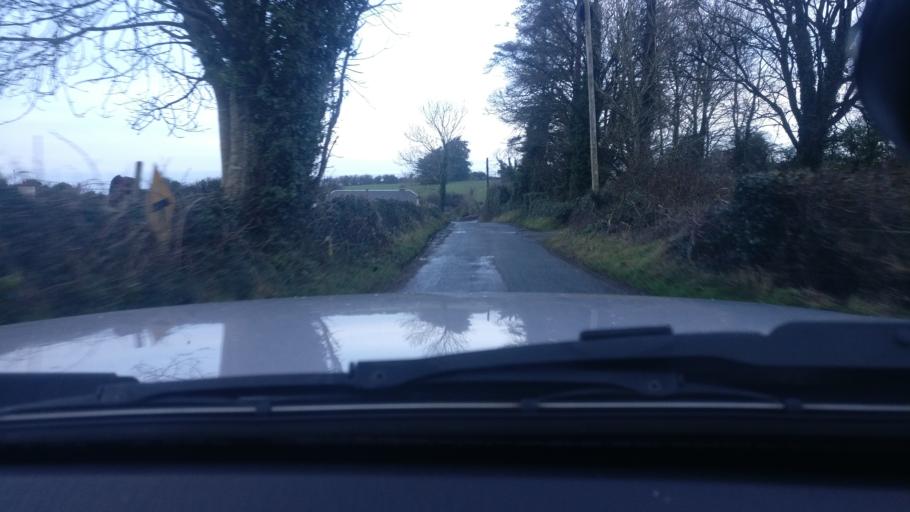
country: IE
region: Connaught
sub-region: County Galway
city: Loughrea
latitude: 53.1704
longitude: -8.5844
